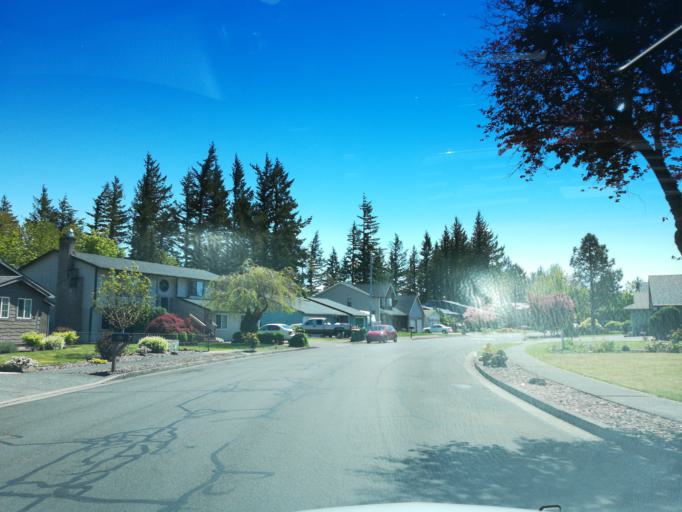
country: US
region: Oregon
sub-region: Multnomah County
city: Troutdale
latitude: 45.5285
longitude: -122.3746
